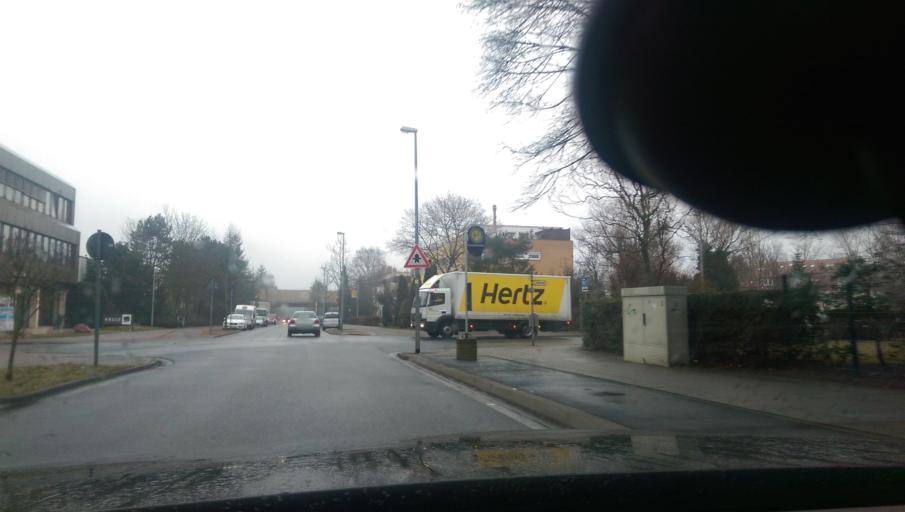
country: DE
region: Lower Saxony
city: Laatzen
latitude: 52.3505
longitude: 9.8209
